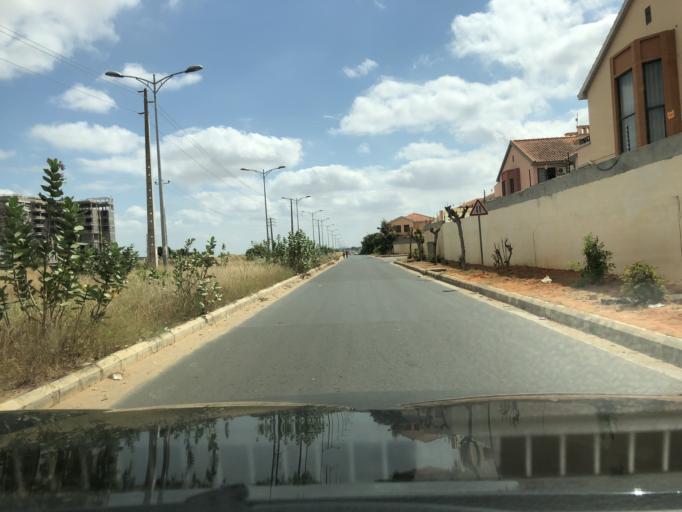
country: AO
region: Luanda
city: Luanda
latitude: -8.9531
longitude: 13.2426
